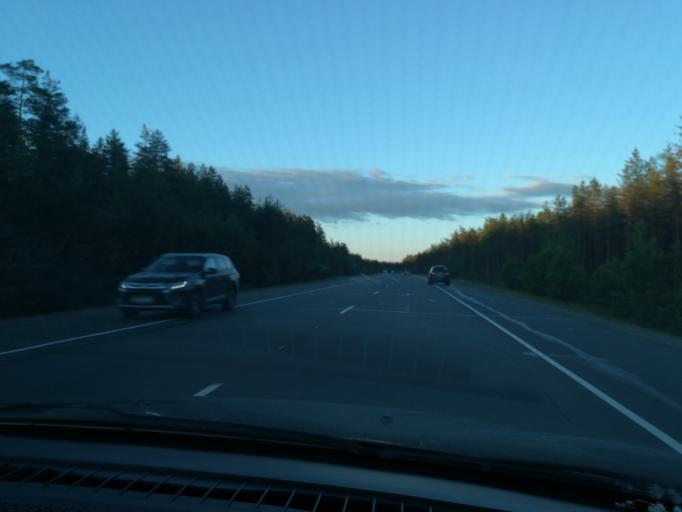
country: RU
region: Leningrad
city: Roshchino
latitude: 60.3601
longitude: 29.5888
